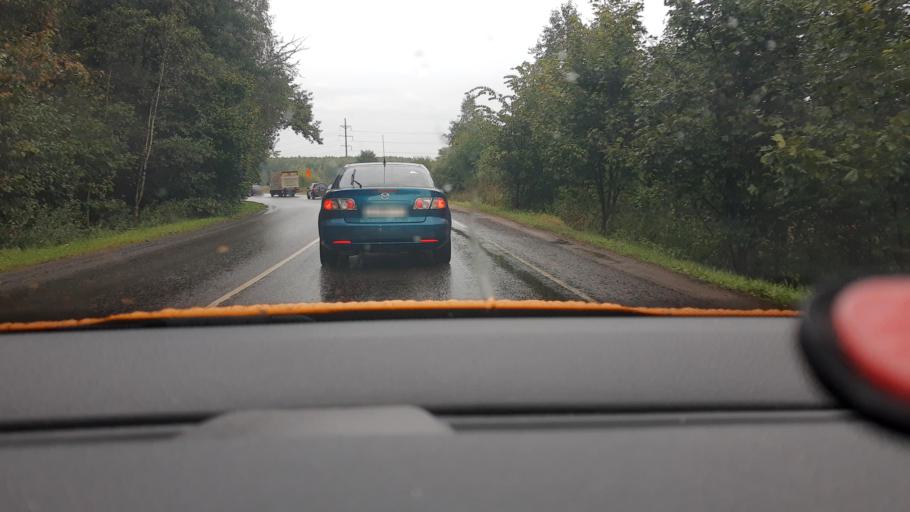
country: RU
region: Moskovskaya
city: Obukhovo
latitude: 55.8009
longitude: 38.2660
